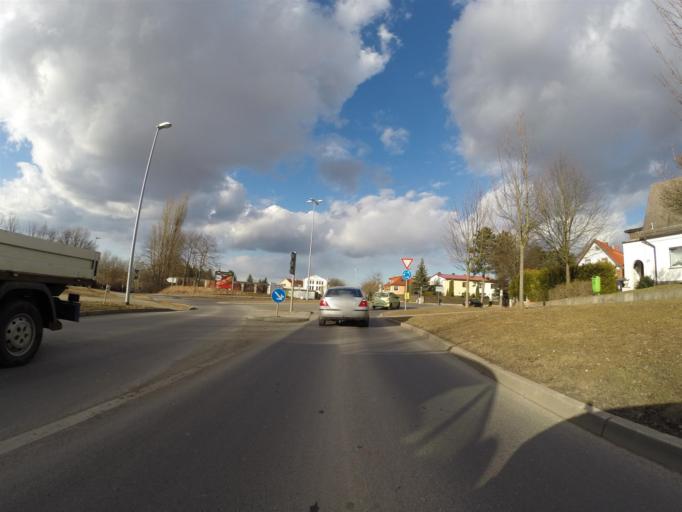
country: DE
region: Thuringia
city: Apolda
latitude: 51.0154
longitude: 11.5132
